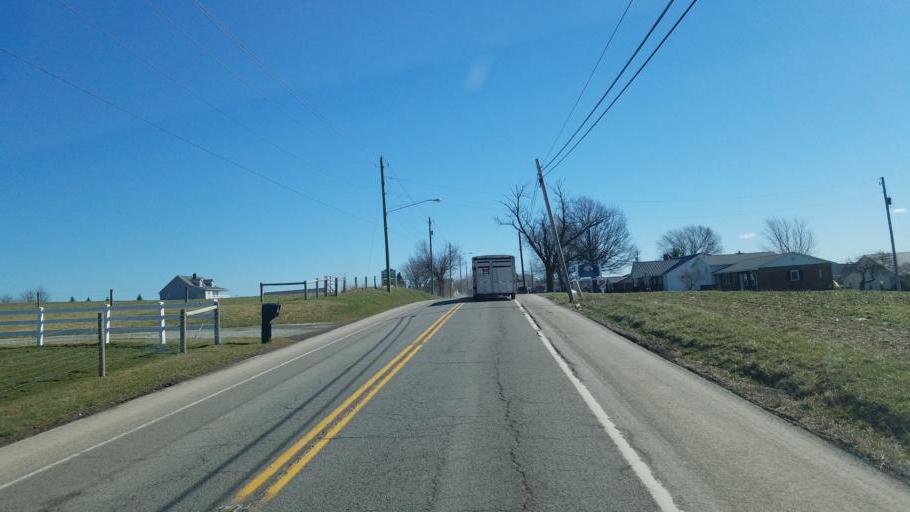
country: US
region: Ohio
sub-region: Wayne County
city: Apple Creek
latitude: 40.6241
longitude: -81.7929
